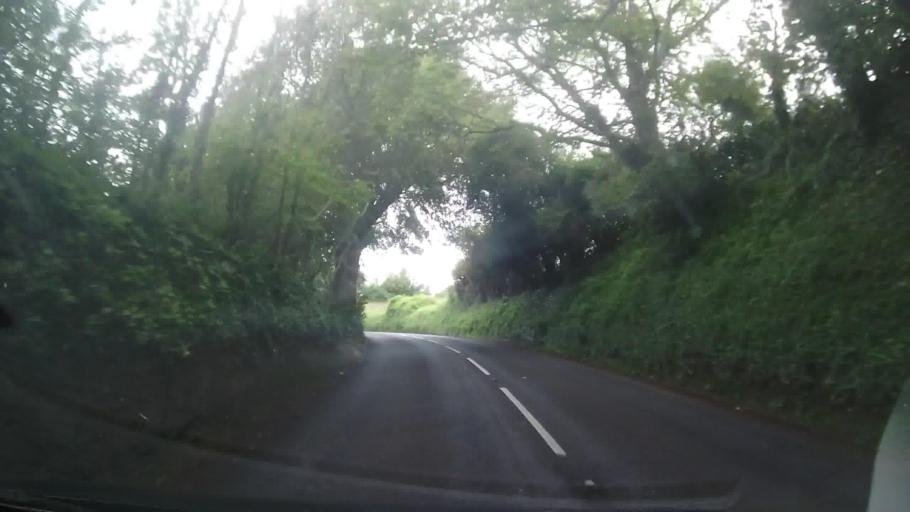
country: GB
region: England
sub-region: Devon
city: Kingsbridge
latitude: 50.2726
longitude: -3.7610
